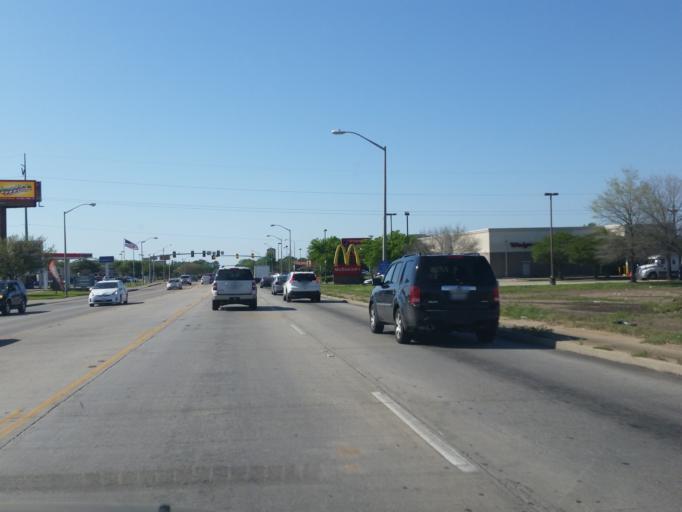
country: US
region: Louisiana
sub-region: Lafayette Parish
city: Milton
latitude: 30.1554
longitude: -92.0469
